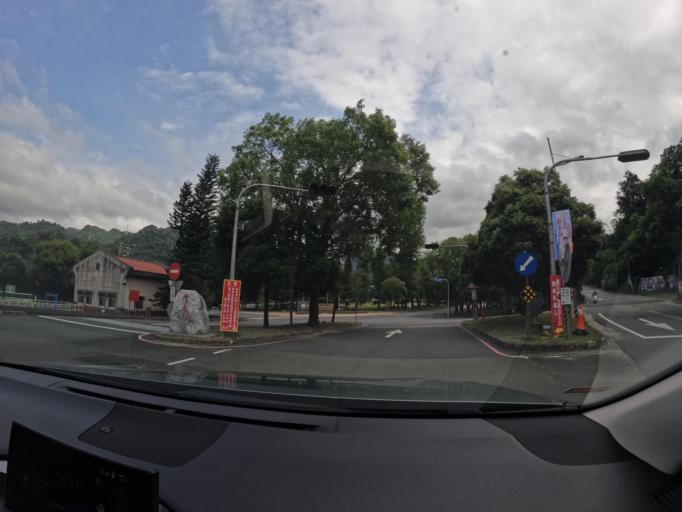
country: TW
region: Taiwan
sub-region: Miaoli
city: Miaoli
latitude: 24.4523
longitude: 120.8765
